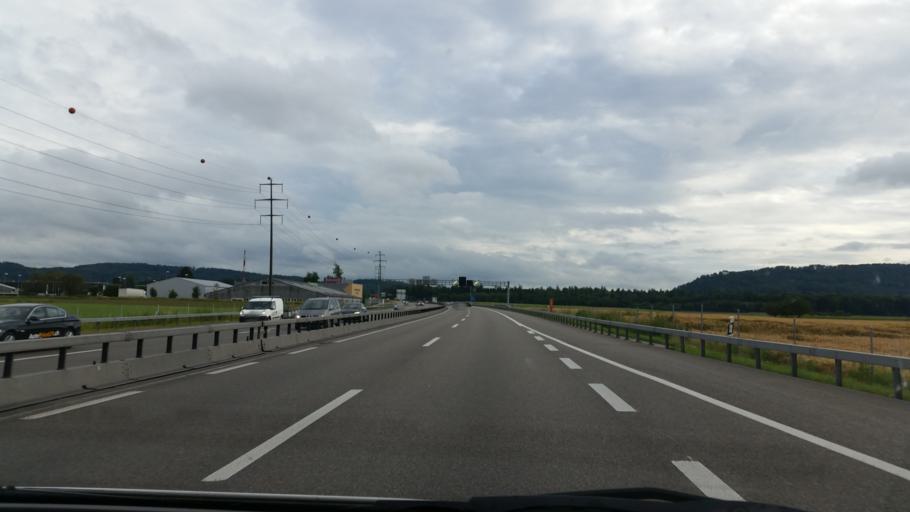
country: CH
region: Aargau
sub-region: Bezirk Baden
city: Birmenstorf
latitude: 47.4427
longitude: 8.2433
